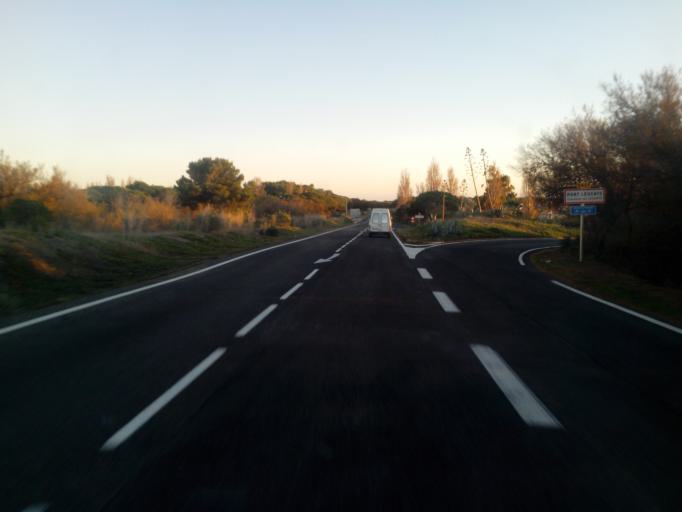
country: FR
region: Languedoc-Roussillon
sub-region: Departement de l'Aude
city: Leucate
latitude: 42.8517
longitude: 3.0355
